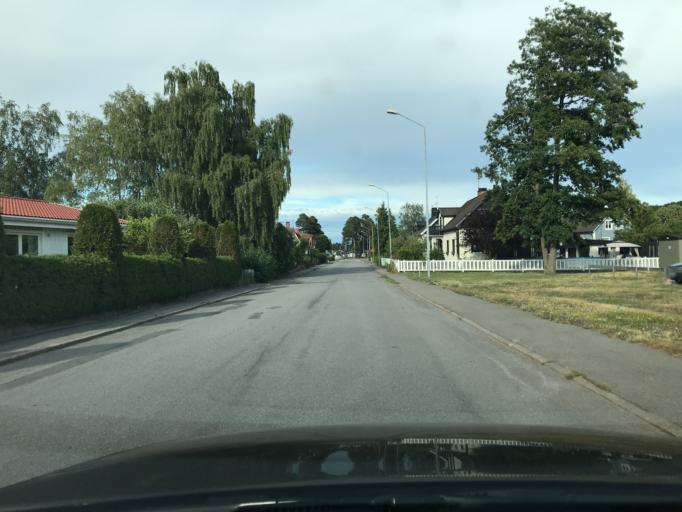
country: SE
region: Kalmar
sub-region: Hultsfreds Kommun
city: Hultsfred
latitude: 57.4964
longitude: 15.8449
